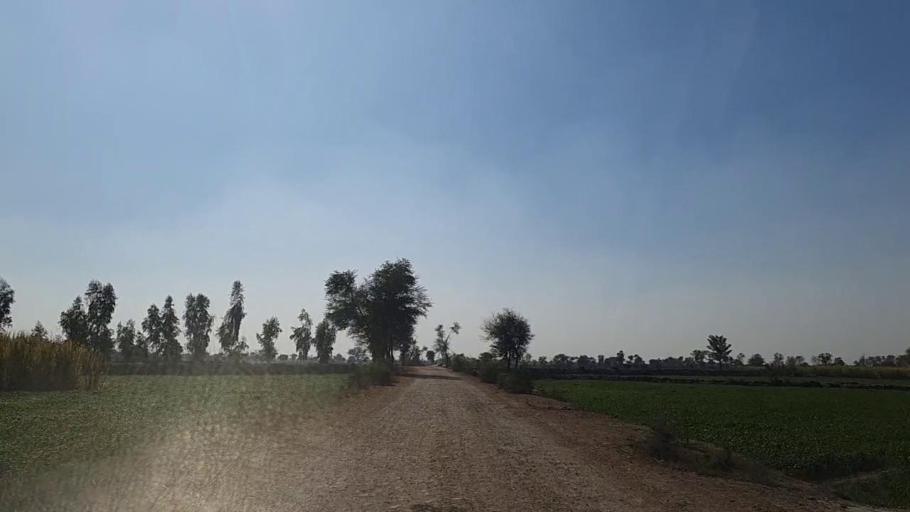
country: PK
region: Sindh
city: Bandhi
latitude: 26.5254
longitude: 68.2912
